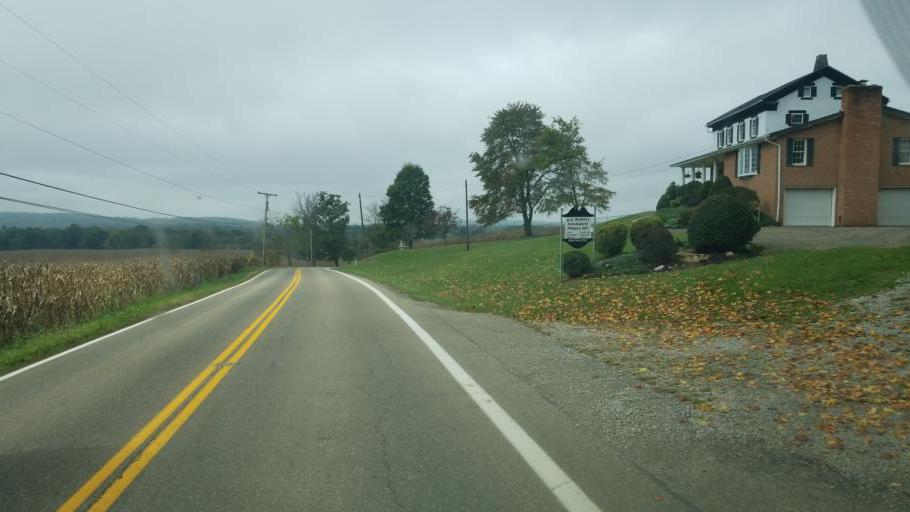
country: US
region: Ohio
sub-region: Stark County
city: Beach City
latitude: 40.6479
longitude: -81.5352
